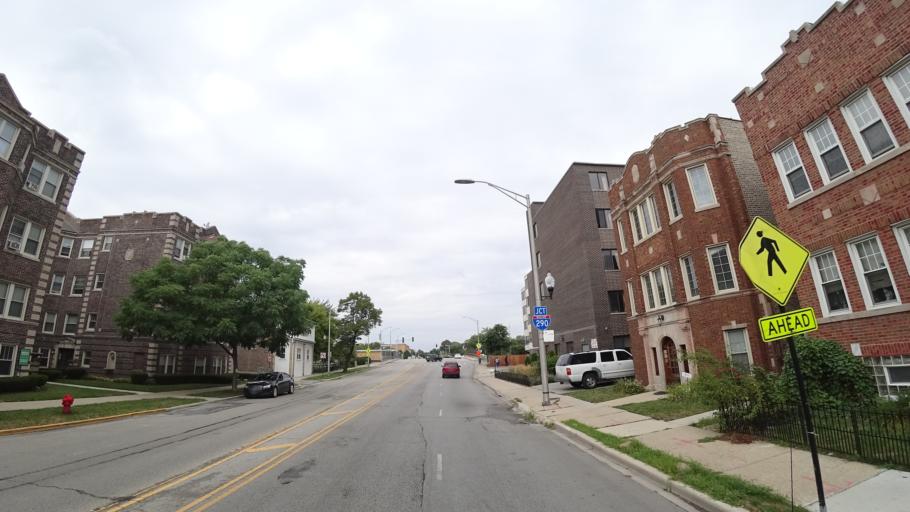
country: US
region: Illinois
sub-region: Cook County
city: Oak Park
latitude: 41.8696
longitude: -87.7742
